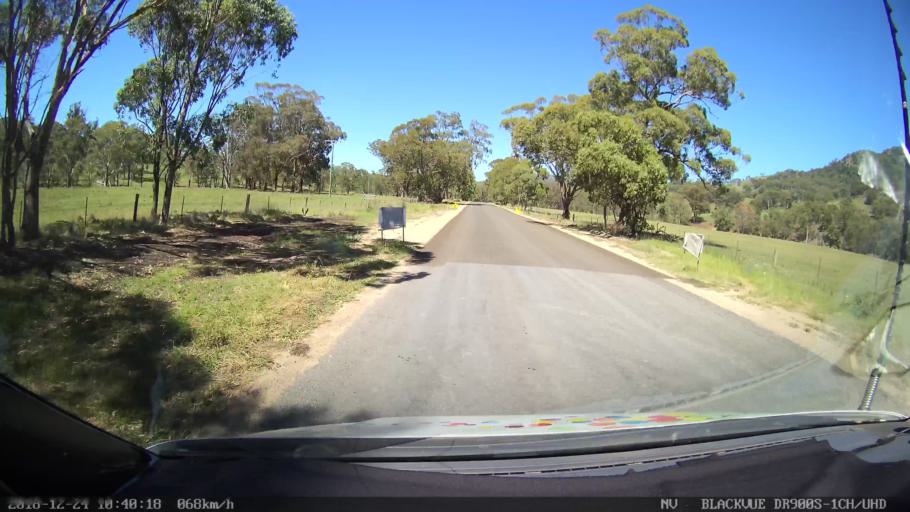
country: AU
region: New South Wales
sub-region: Upper Hunter Shire
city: Merriwa
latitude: -31.8609
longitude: 150.4685
